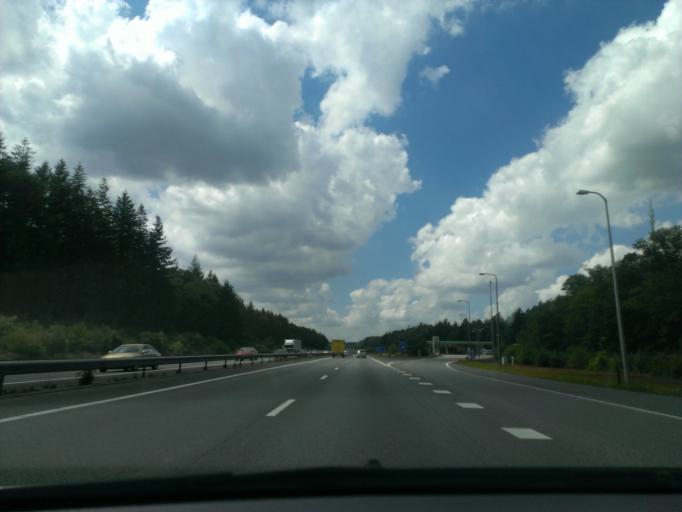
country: NL
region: Gelderland
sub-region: Gemeente Apeldoorn
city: Beekbergen
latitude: 52.1846
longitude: 5.8950
